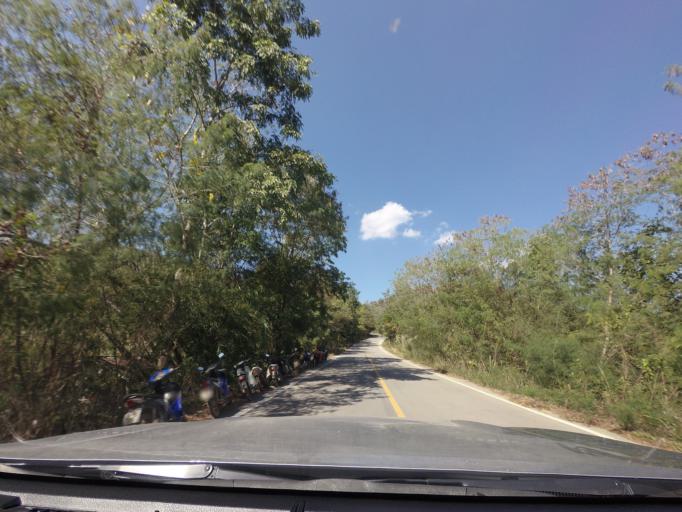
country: TH
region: Lampang
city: Chae Hom
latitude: 18.5429
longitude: 99.6384
